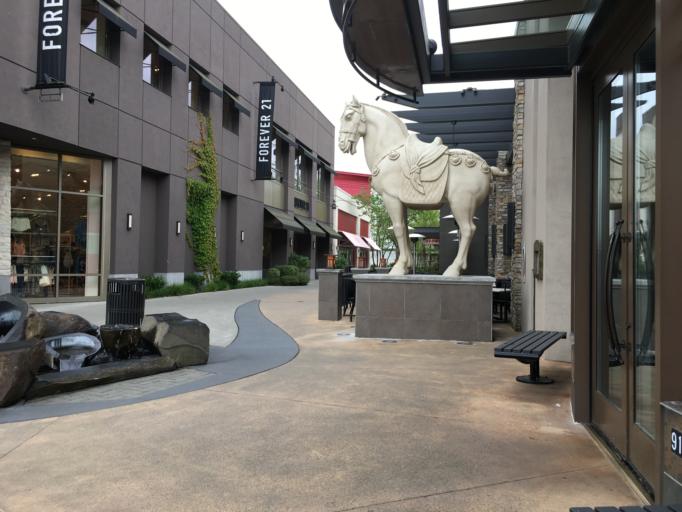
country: US
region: Washington
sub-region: Snohomish County
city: Alderwood Manor
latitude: 47.8309
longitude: -122.2703
